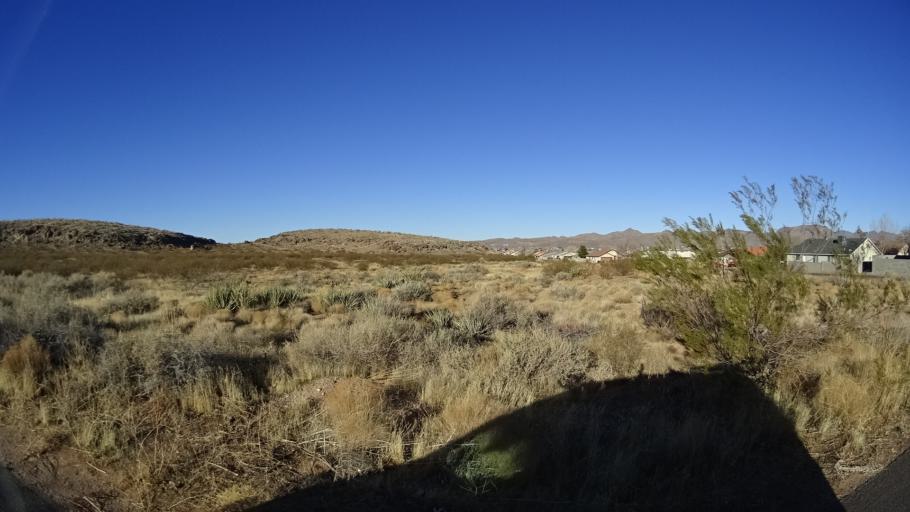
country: US
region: Arizona
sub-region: Mohave County
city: Kingman
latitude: 35.2102
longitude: -114.0022
